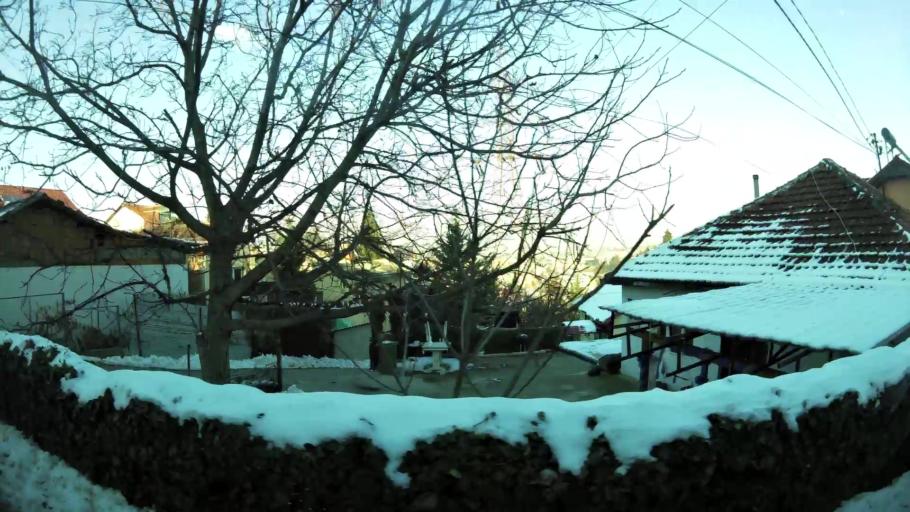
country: MK
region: Karpos
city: Skopje
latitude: 41.9903
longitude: 21.4025
